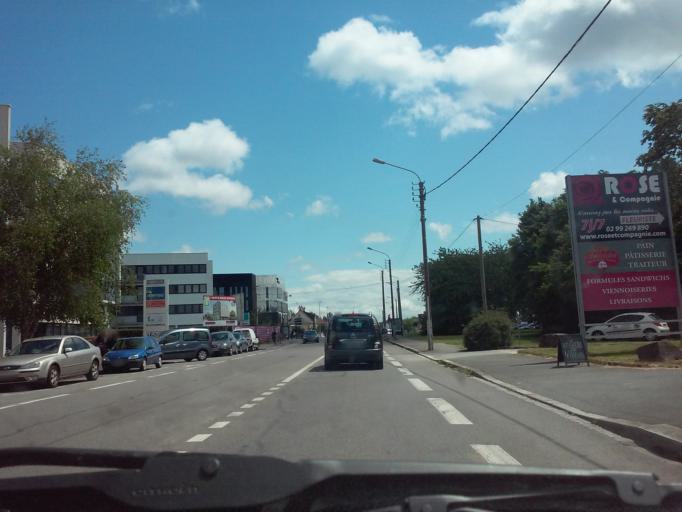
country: FR
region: Brittany
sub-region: Departement d'Ille-et-Vilaine
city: Chantepie
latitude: 48.0947
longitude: -1.6360
